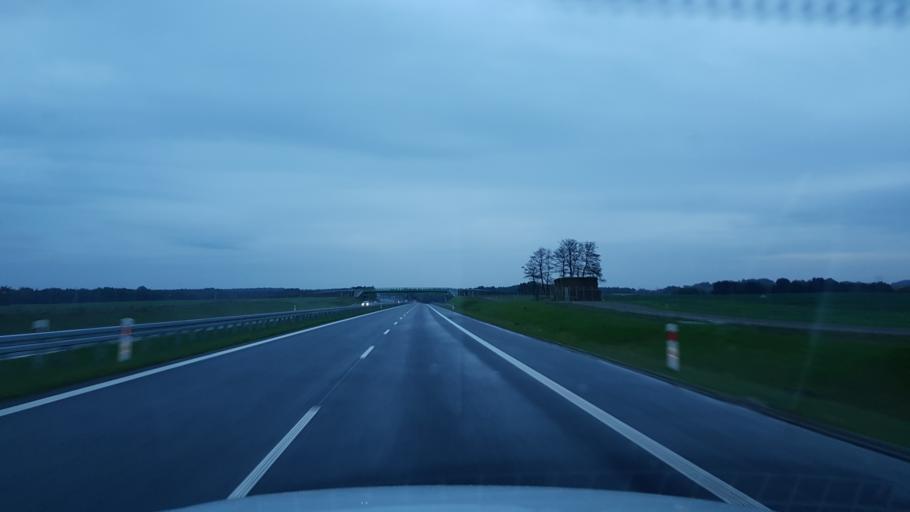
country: PL
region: West Pomeranian Voivodeship
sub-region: Powiat gryficki
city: Brojce
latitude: 53.9220
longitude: 15.3853
